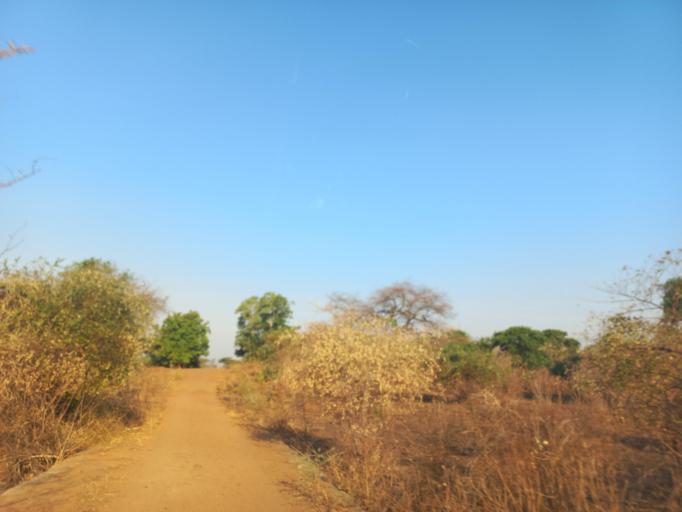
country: ZM
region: Lusaka
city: Luangwa
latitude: -15.4214
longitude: 30.2790
